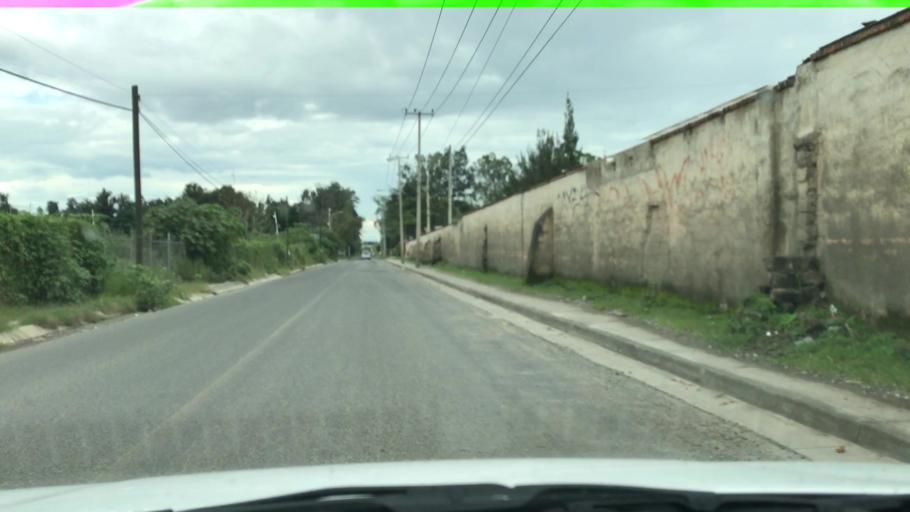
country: MX
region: Jalisco
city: Nicolas R Casillas
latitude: 20.5443
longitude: -103.4870
